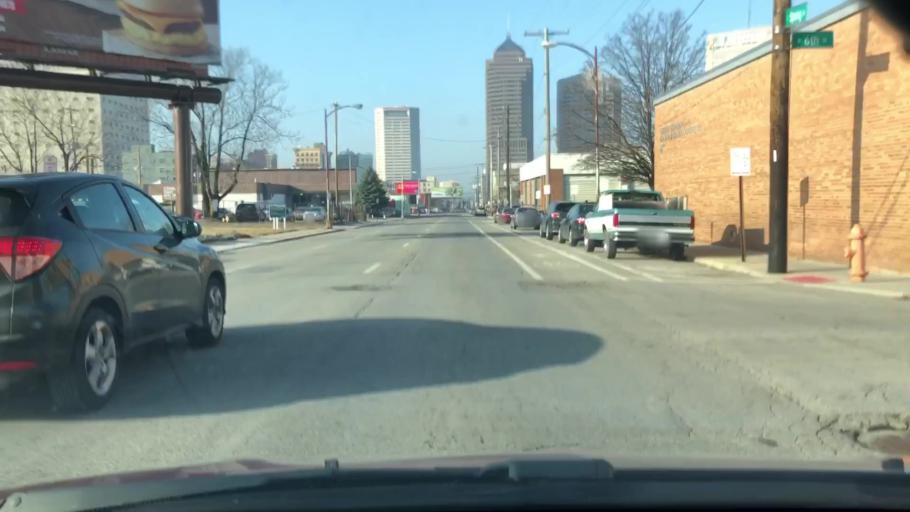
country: US
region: Ohio
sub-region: Franklin County
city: Columbus
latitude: 39.9671
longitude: -82.9931
